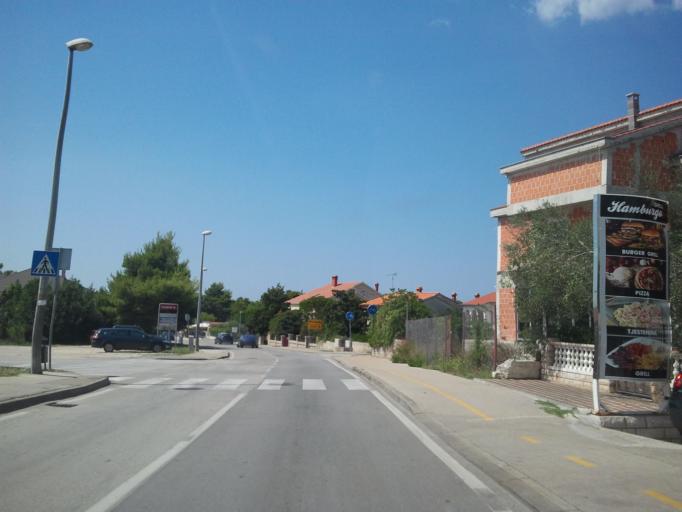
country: HR
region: Zadarska
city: Zadar
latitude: 44.1362
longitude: 15.2196
